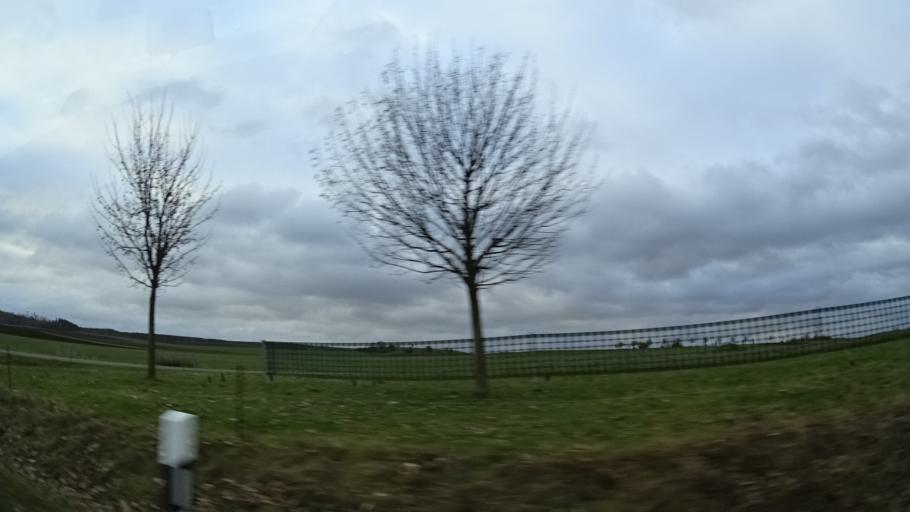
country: DE
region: Thuringia
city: Neustadt (Orla)
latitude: 50.7314
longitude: 11.7700
